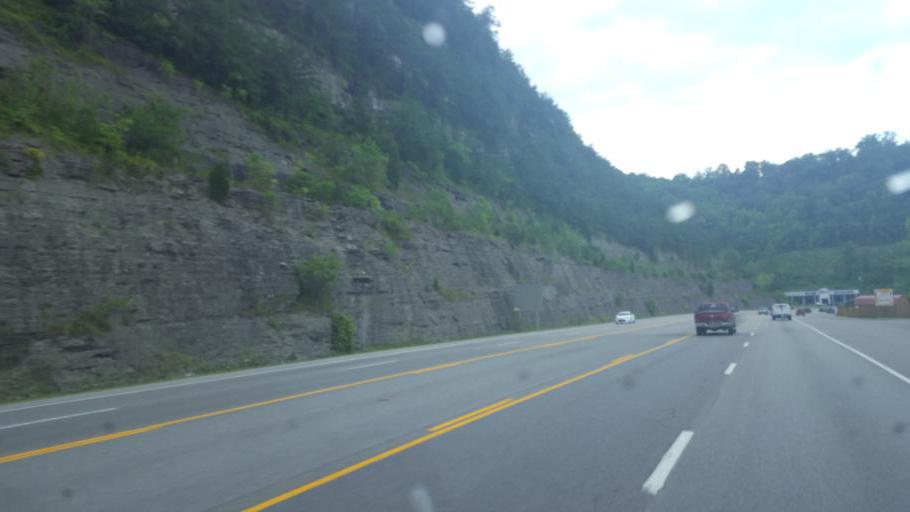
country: US
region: Kentucky
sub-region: Pike County
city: Pikeville
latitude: 37.4991
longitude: -82.5315
